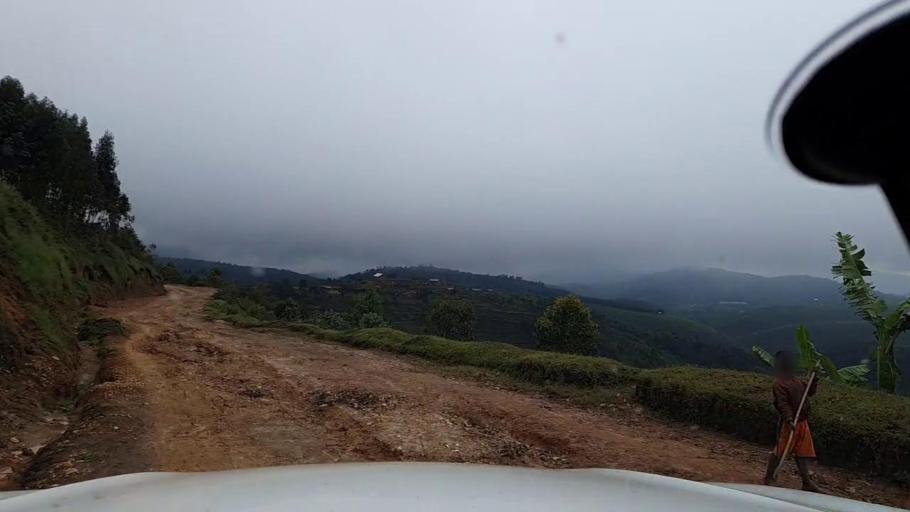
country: RW
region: Western Province
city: Kibuye
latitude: -2.0838
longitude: 29.5046
